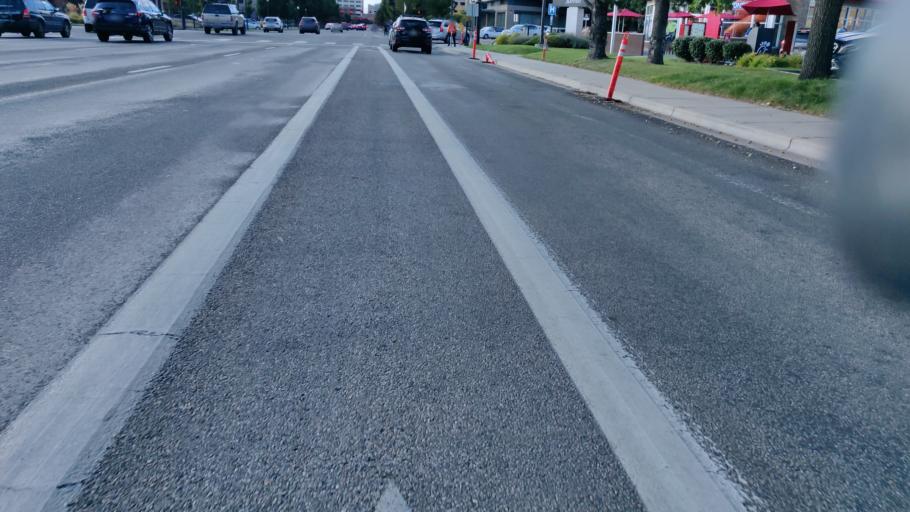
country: US
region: Idaho
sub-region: Ada County
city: Boise
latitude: 43.6077
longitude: -116.1927
